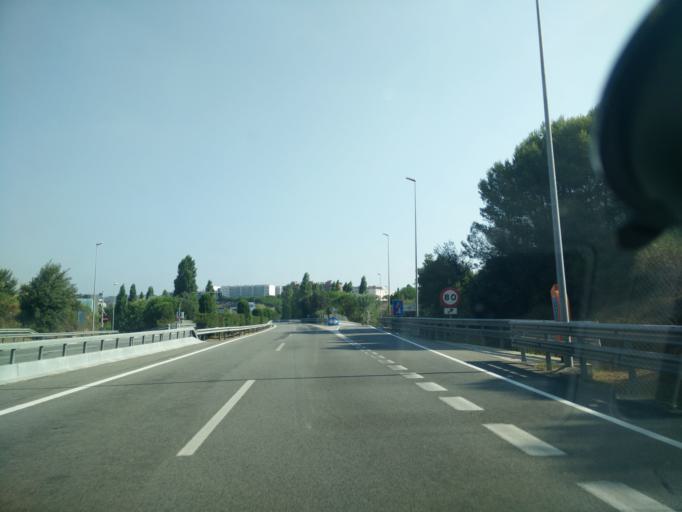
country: ES
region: Catalonia
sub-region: Provincia de Barcelona
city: Sant Cugat del Valles
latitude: 41.4770
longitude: 2.0655
